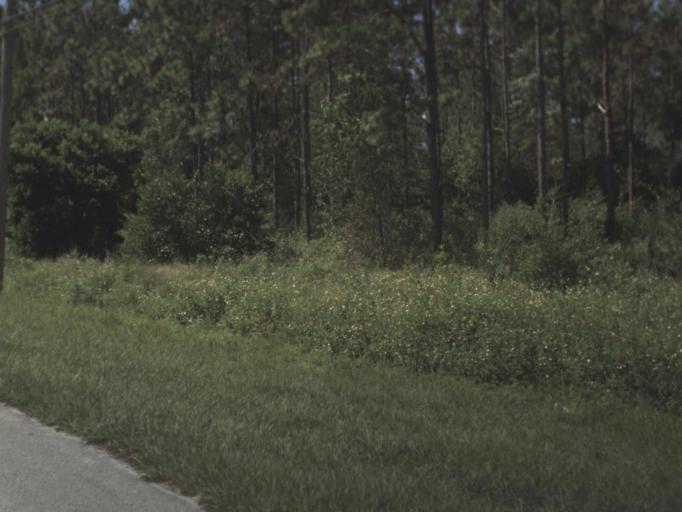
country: US
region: Florida
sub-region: Polk County
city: Lake Hamilton
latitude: 28.0780
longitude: -81.6202
